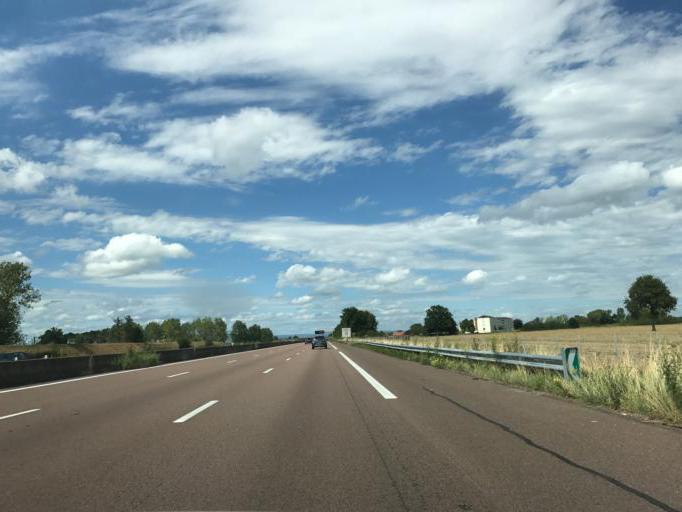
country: FR
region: Bourgogne
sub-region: Departement de Saone-et-Loire
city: Sevrey
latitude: 46.7263
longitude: 4.8375
